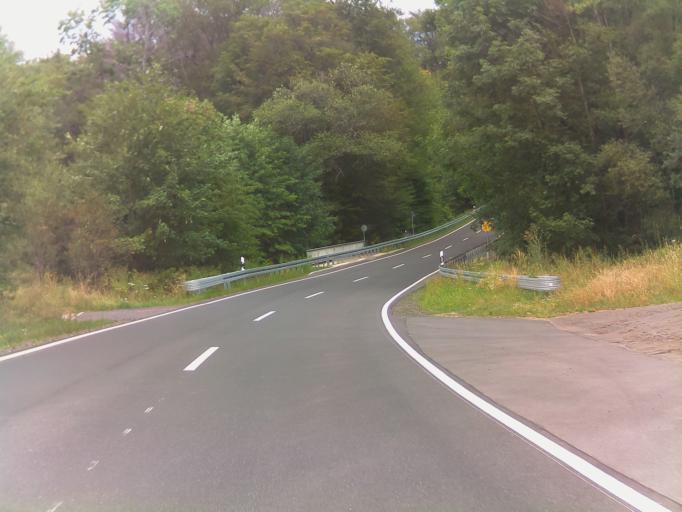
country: DE
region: Hesse
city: Gedern
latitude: 50.4367
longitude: 9.2732
